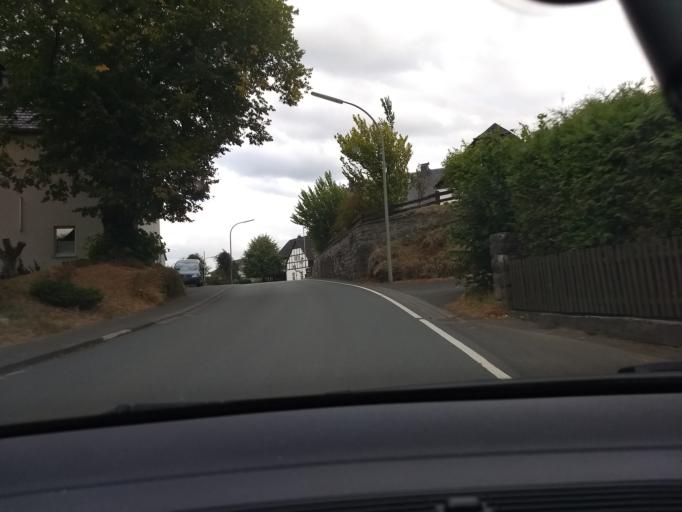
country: DE
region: North Rhine-Westphalia
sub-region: Regierungsbezirk Arnsberg
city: Arnsberg
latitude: 51.3325
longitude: 8.1325
